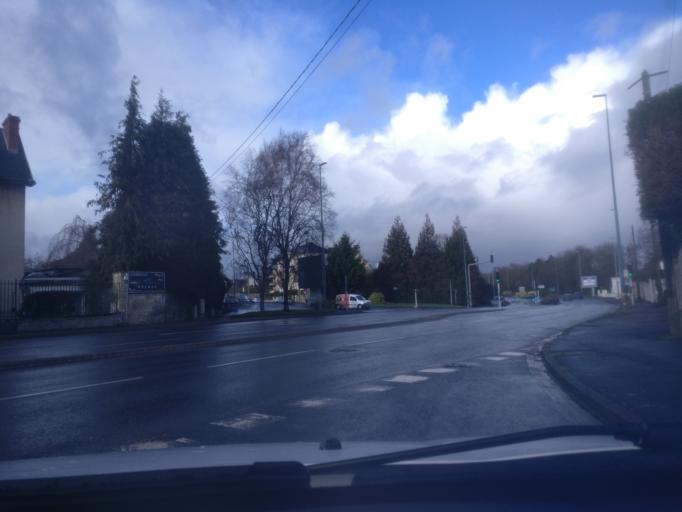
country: FR
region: Lower Normandy
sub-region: Departement du Calvados
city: Caen
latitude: 49.1919
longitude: -0.3751
